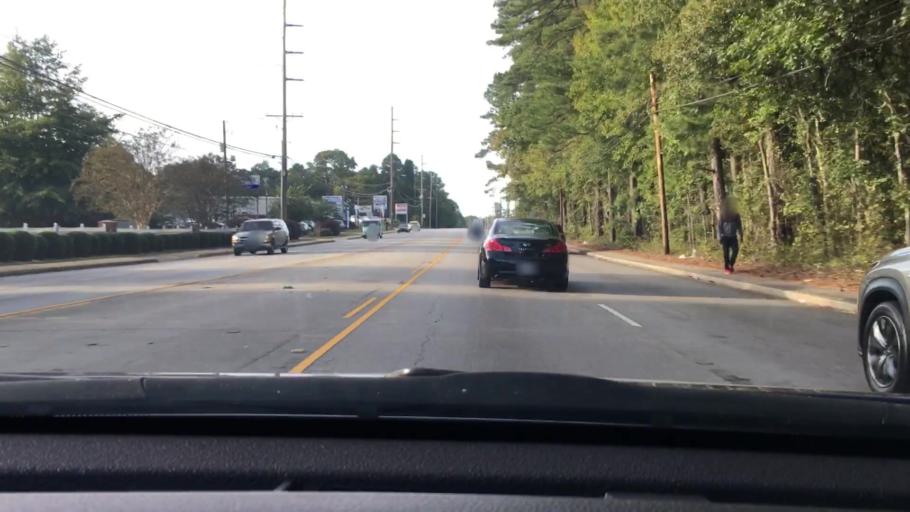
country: US
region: South Carolina
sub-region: Lexington County
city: Saint Andrews
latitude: 34.0611
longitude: -81.1135
